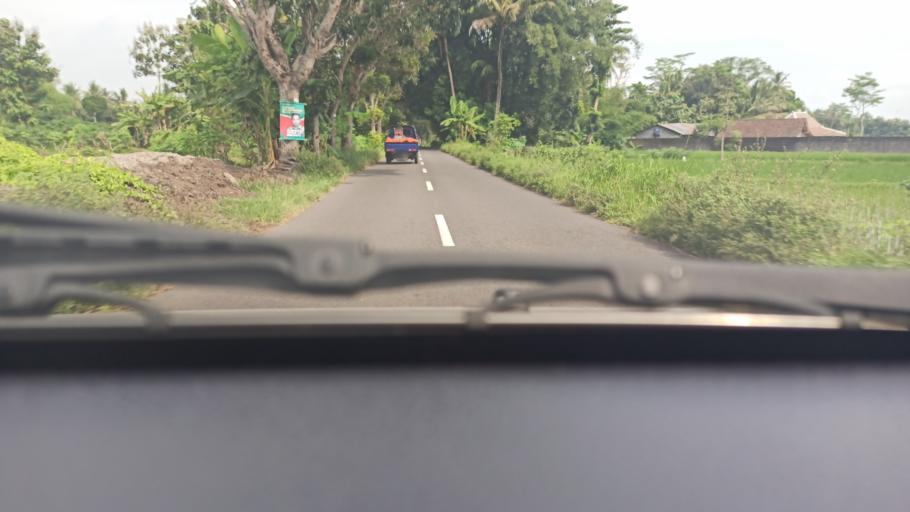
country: ID
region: Daerah Istimewa Yogyakarta
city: Sleman
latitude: -7.6931
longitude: 110.2987
